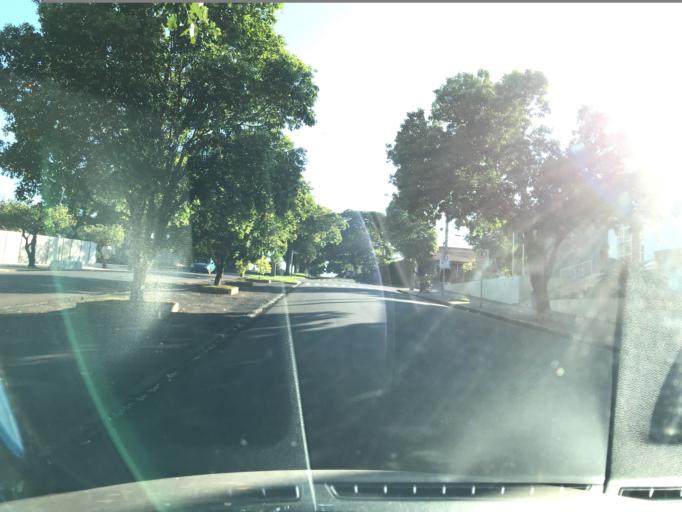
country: BR
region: Parana
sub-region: Ipora
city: Ipora
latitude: -24.0015
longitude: -53.7144
